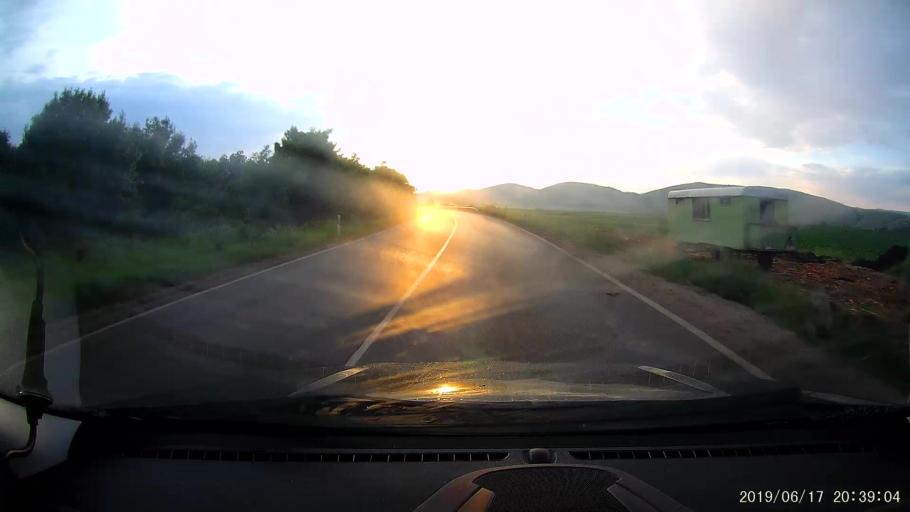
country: BG
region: Sofiya
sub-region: Obshtina Slivnitsa
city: Slivnitsa
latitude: 42.8808
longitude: 23.0154
